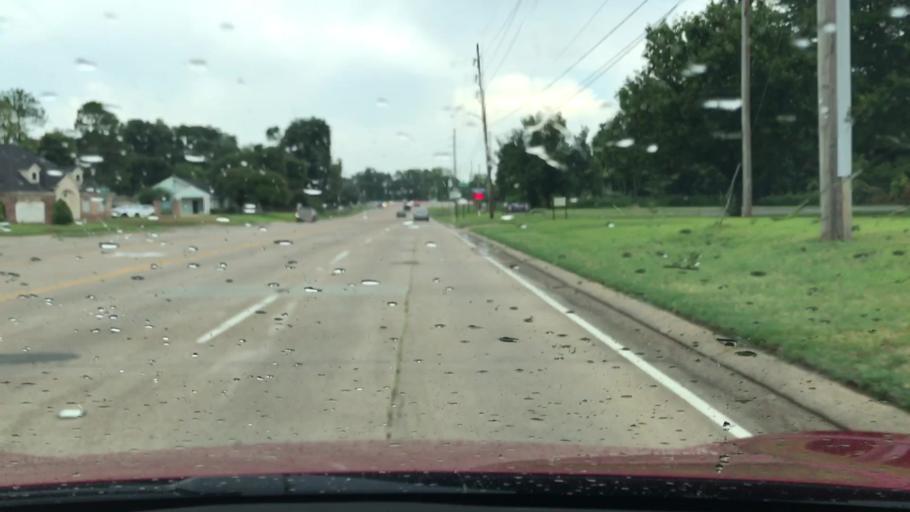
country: US
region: Louisiana
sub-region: Bossier Parish
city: Bossier City
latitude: 32.4449
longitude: -93.7061
